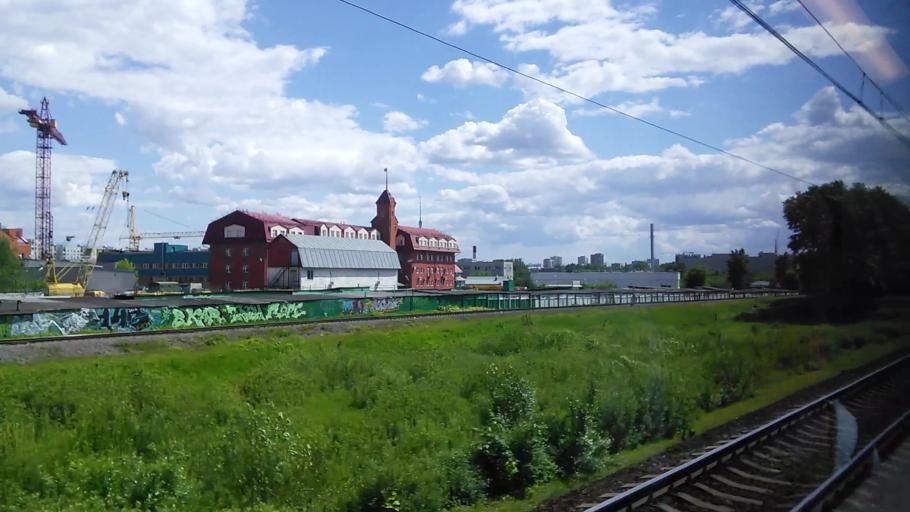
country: RU
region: Moscow
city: Likhobory
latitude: 55.8585
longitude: 37.5743
